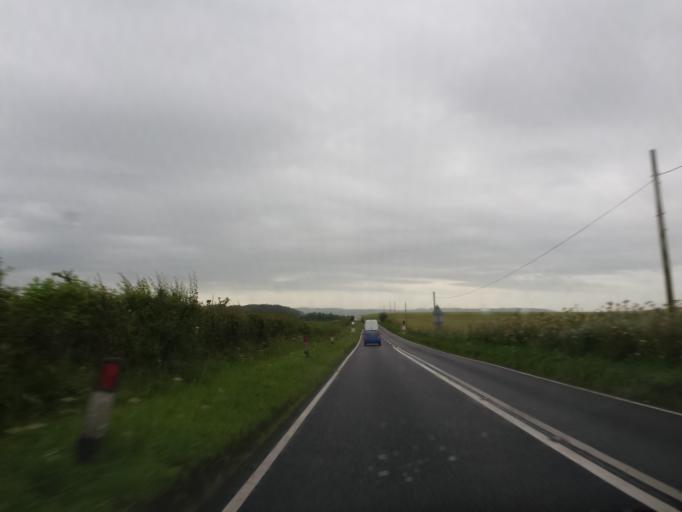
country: GB
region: Scotland
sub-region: Fife
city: Balmullo
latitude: 56.4023
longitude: -2.9120
